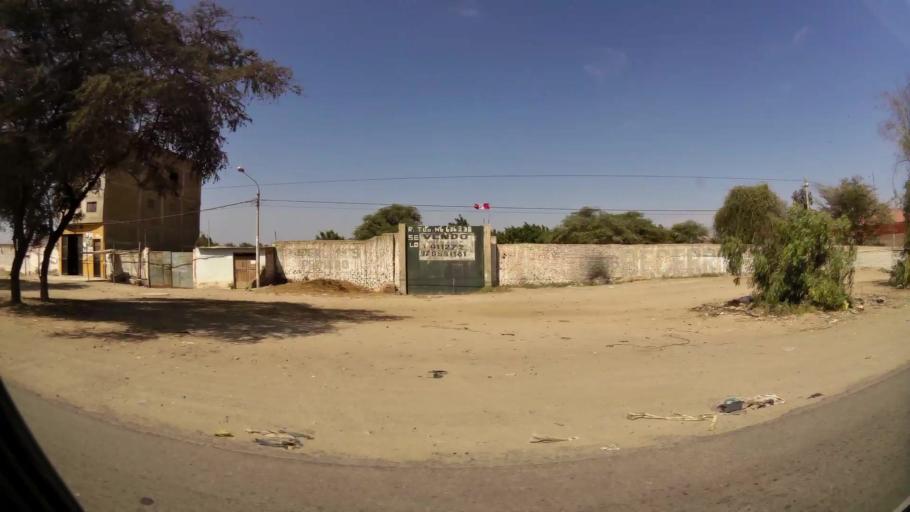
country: PE
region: Lambayeque
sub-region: Provincia de Chiclayo
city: Reque
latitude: -6.8242
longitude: -79.8294
